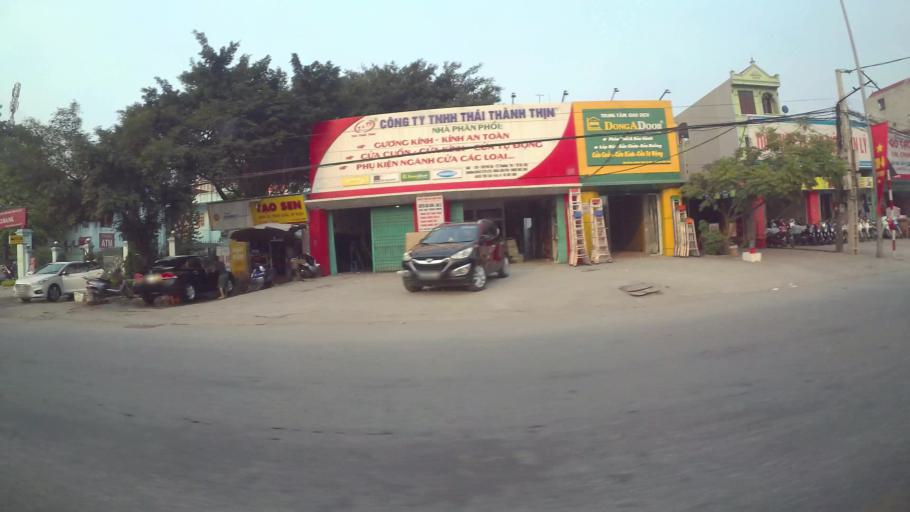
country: VN
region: Ha Noi
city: Thuong Tin
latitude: 20.8730
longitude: 105.8637
